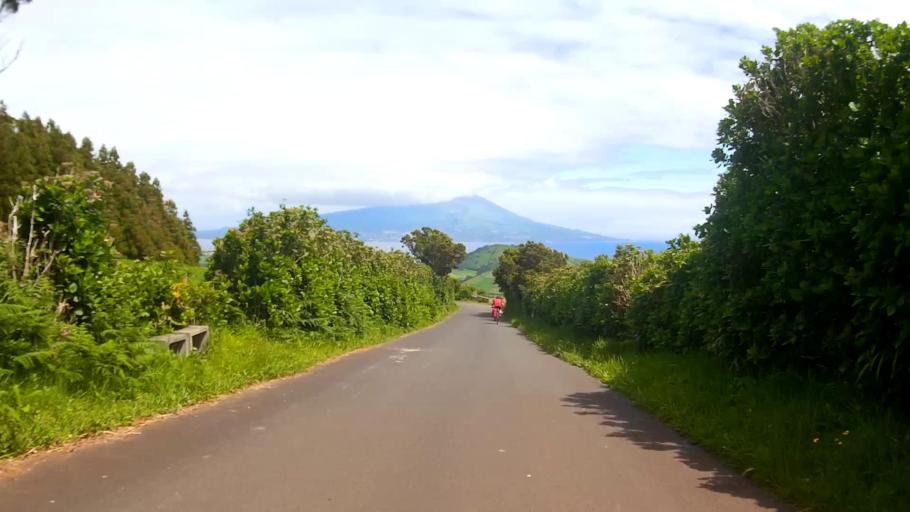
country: PT
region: Azores
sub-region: Horta
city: Horta
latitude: 38.5513
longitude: -28.6714
